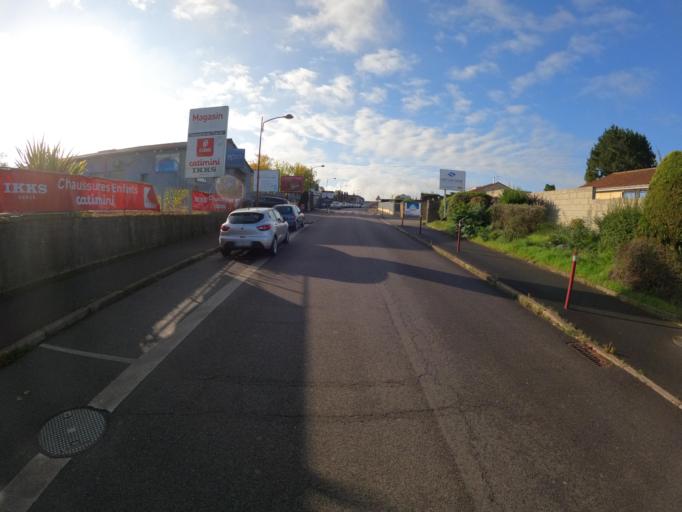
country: FR
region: Pays de la Loire
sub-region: Departement de Maine-et-Loire
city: La Seguiniere
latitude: 47.0574
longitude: -0.9394
